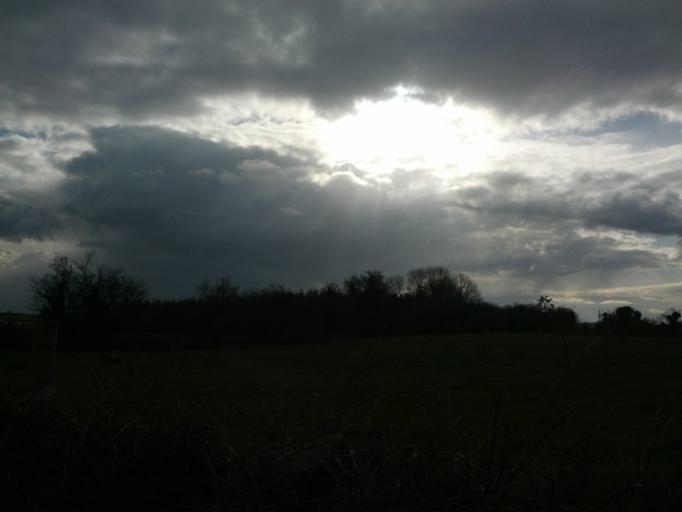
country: IE
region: Connaught
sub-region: County Galway
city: Athenry
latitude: 53.4320
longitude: -8.6245
